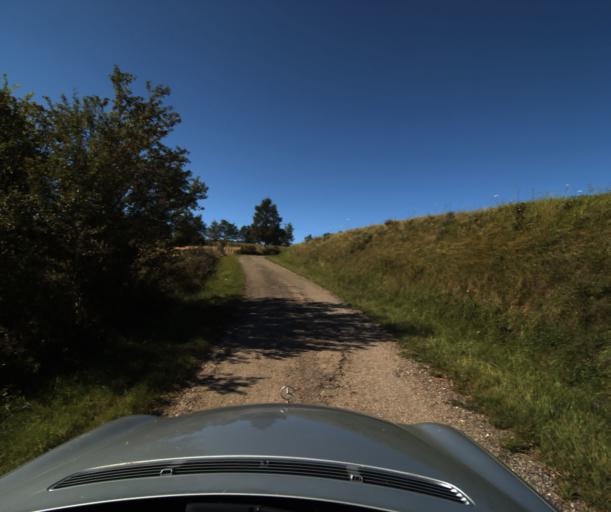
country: FR
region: Midi-Pyrenees
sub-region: Departement de l'Ariege
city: Lavelanet
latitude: 42.9715
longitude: 1.8886
